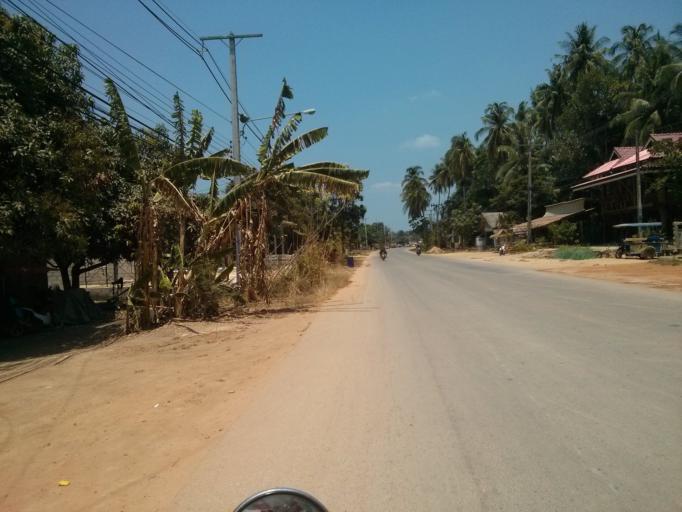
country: TH
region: Krabi
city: Saladan
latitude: 7.5717
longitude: 99.0355
